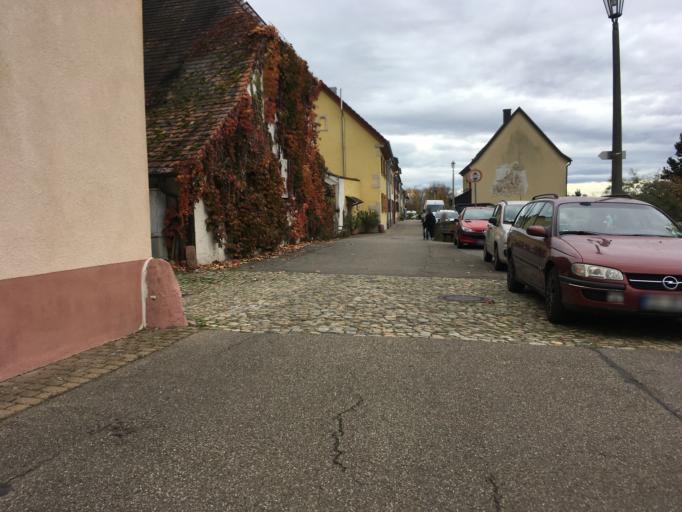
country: DE
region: Baden-Wuerttemberg
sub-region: Freiburg Region
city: Breisach am Rhein
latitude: 48.0311
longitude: 7.5761
